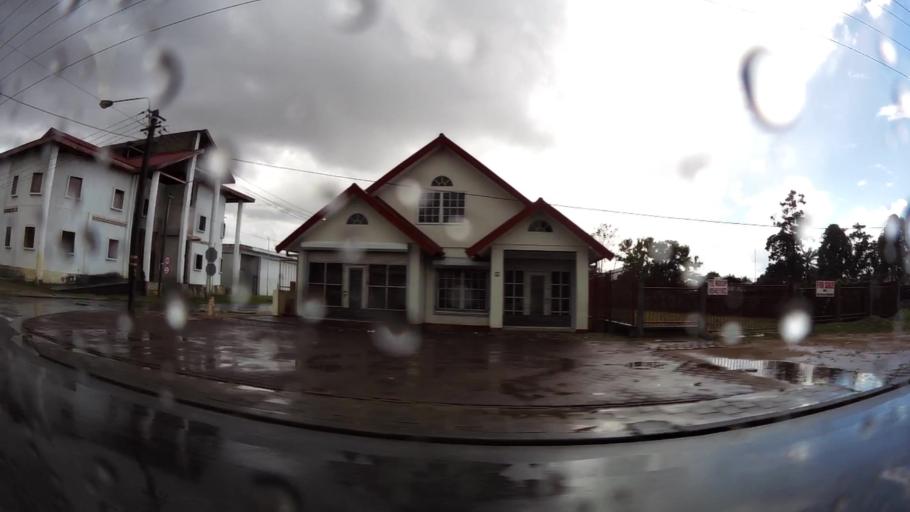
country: SR
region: Paramaribo
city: Paramaribo
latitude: 5.8211
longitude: -55.1734
